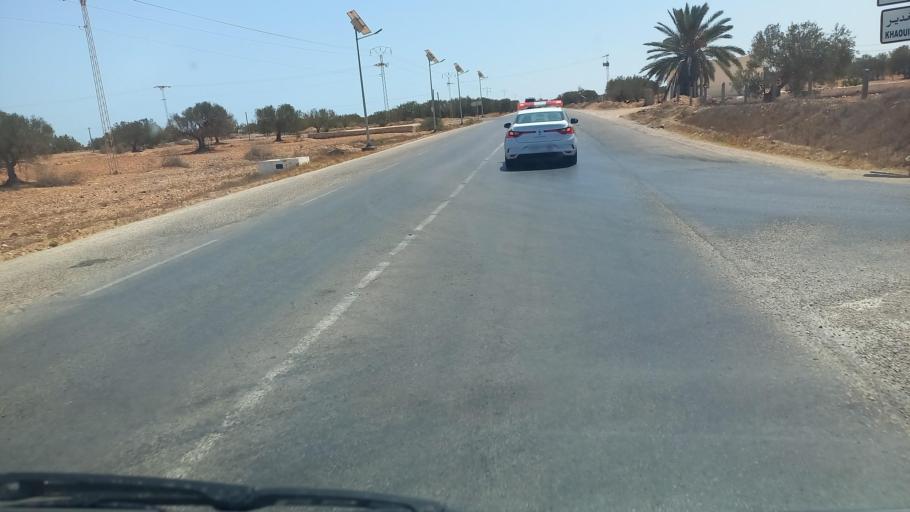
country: TN
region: Madanin
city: Zarzis
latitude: 33.5580
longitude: 11.0580
